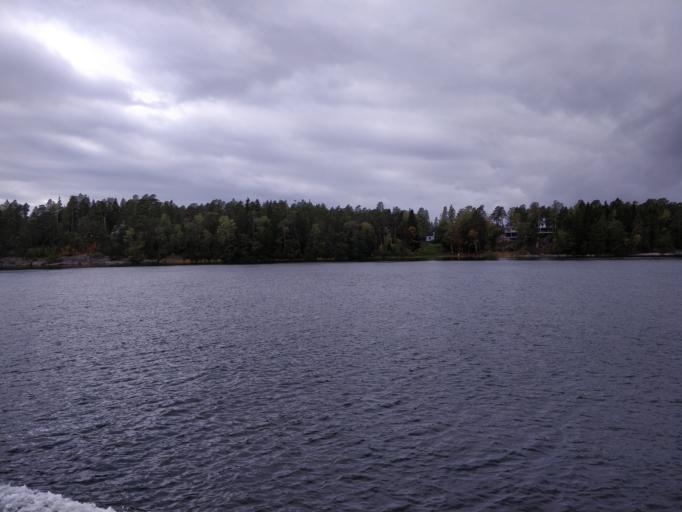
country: FI
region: Uusimaa
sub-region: Helsinki
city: Vantaa
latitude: 60.1672
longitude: 25.0979
